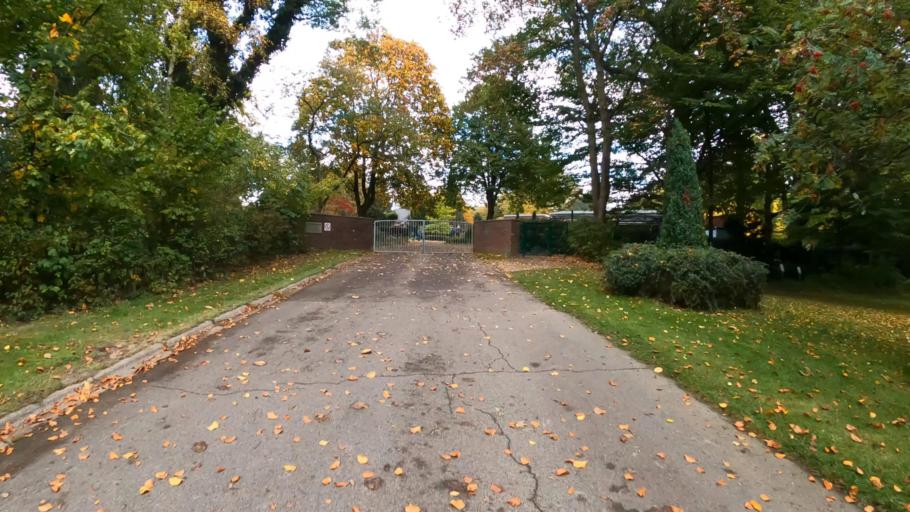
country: DE
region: Schleswig-Holstein
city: Ahrensburg
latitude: 53.6631
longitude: 10.2158
